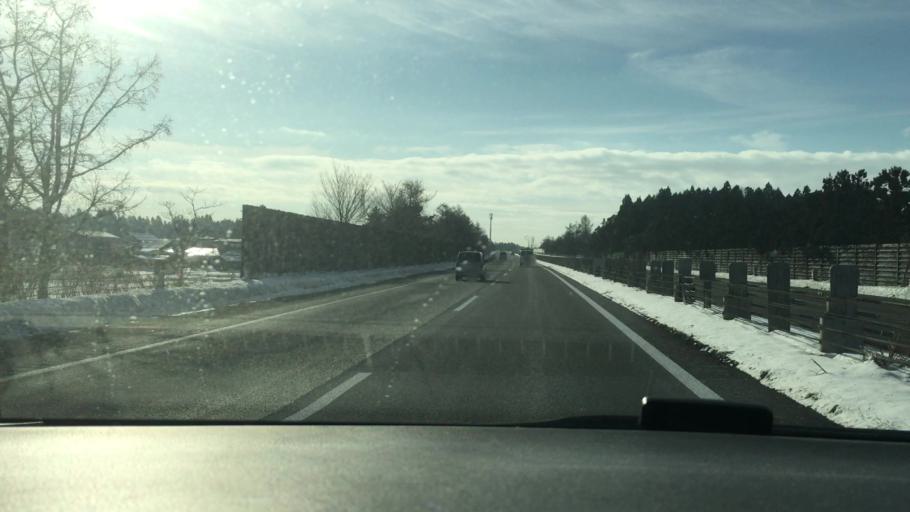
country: JP
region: Iwate
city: Hanamaki
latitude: 39.3499
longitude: 141.0897
